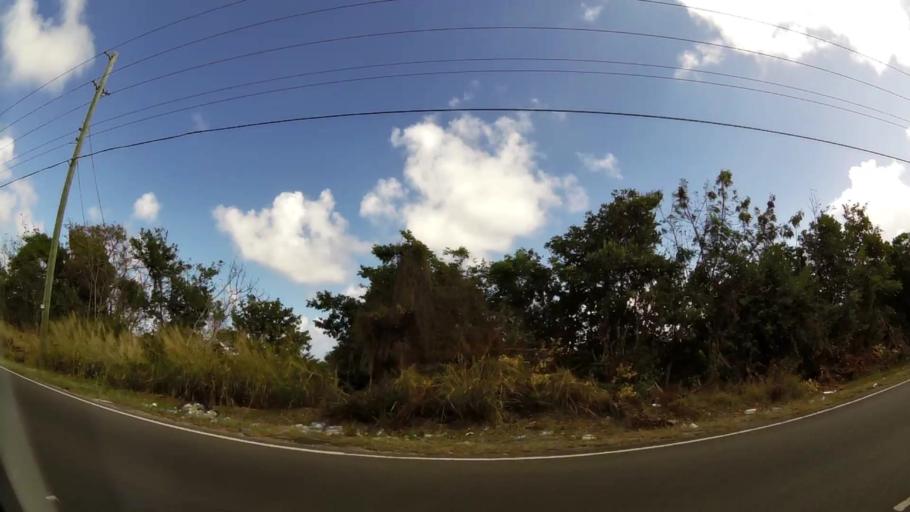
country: LC
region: Micoud Quarter
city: Micoud
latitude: 13.8093
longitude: -60.9022
